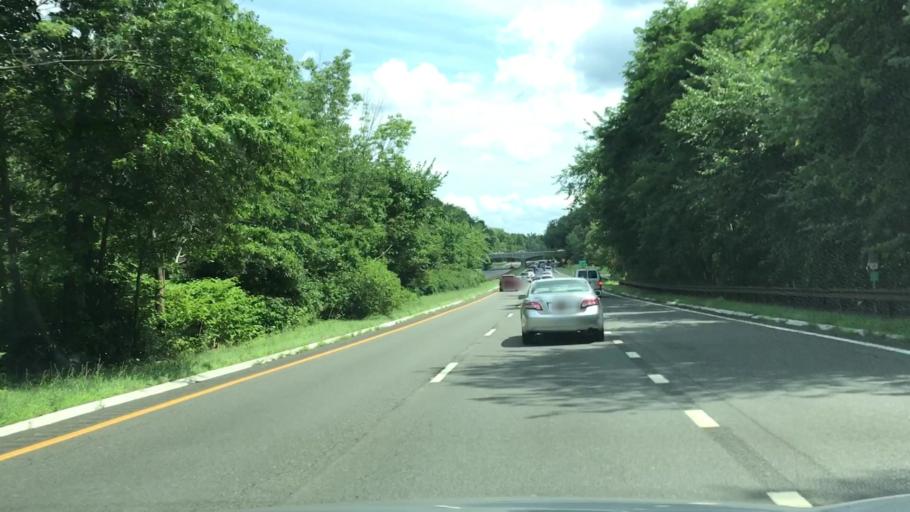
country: US
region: New York
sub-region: Rockland County
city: Bardonia
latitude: 41.1236
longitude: -74.0110
